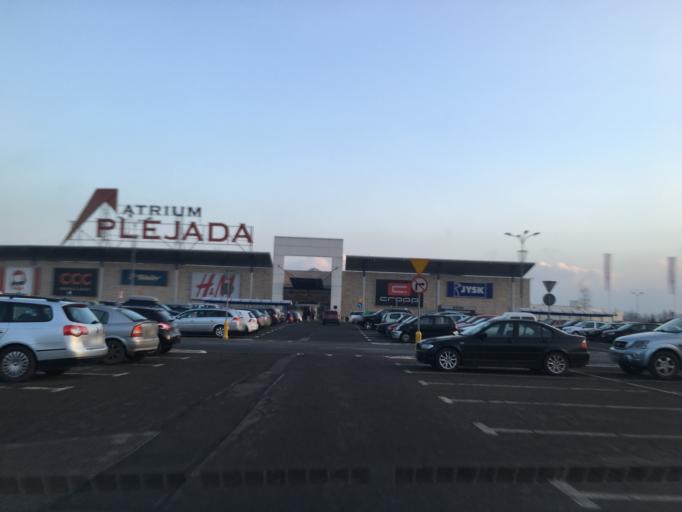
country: PL
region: Silesian Voivodeship
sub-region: Zabrze
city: Zabrze
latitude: 50.3473
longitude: 18.8476
